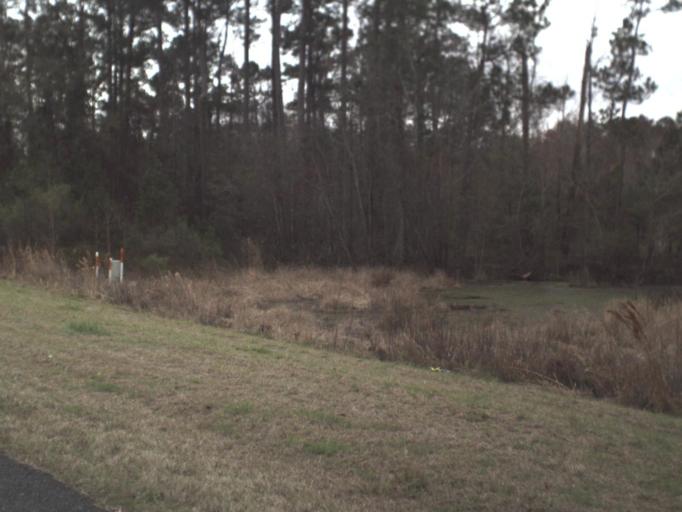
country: US
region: Florida
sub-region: Jefferson County
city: Monticello
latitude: 30.3794
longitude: -83.8174
